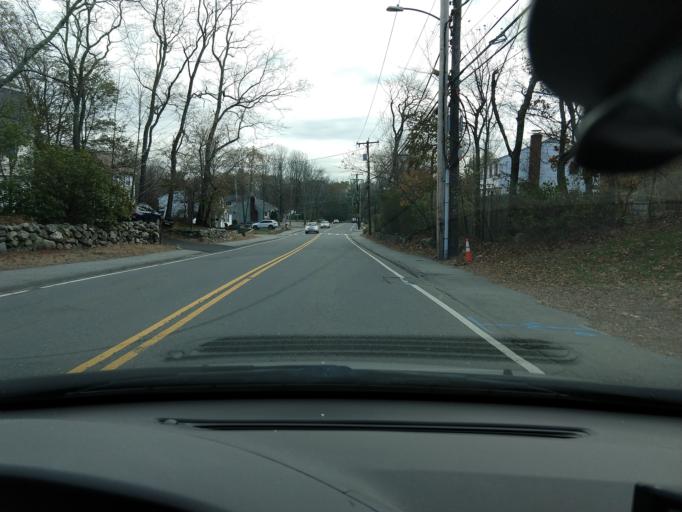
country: US
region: Massachusetts
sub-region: Middlesex County
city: Burlington
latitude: 42.5020
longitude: -71.1900
